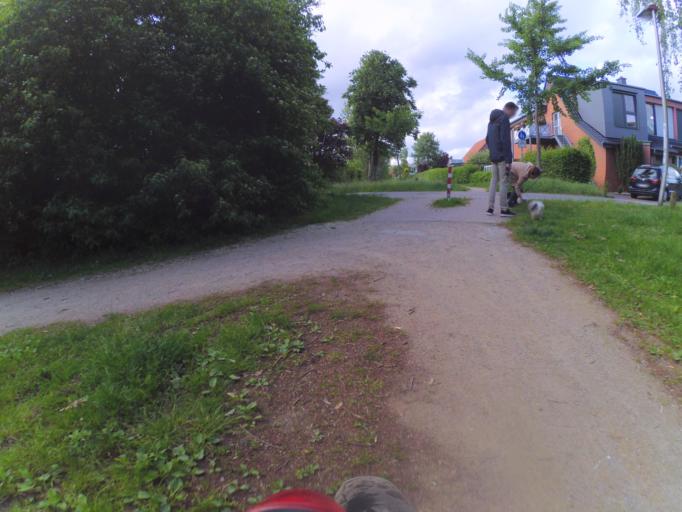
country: DE
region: North Rhine-Westphalia
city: Ibbenburen
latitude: 52.2813
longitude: 7.6989
